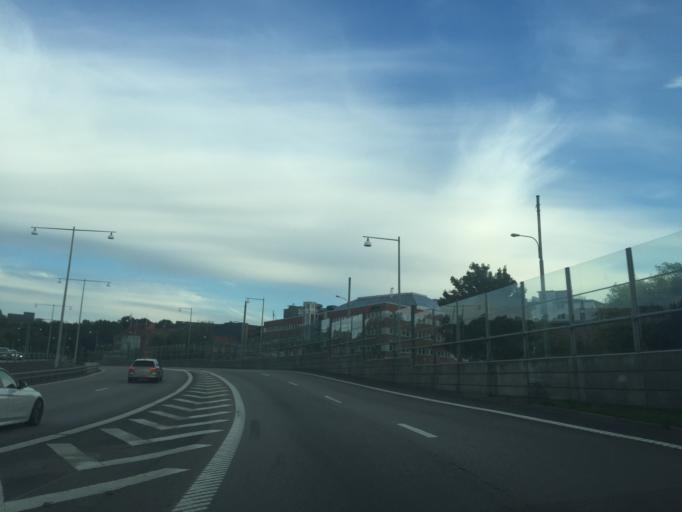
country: SE
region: Vaestra Goetaland
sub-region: Goteborg
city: Goeteborg
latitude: 57.7135
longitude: 11.9941
